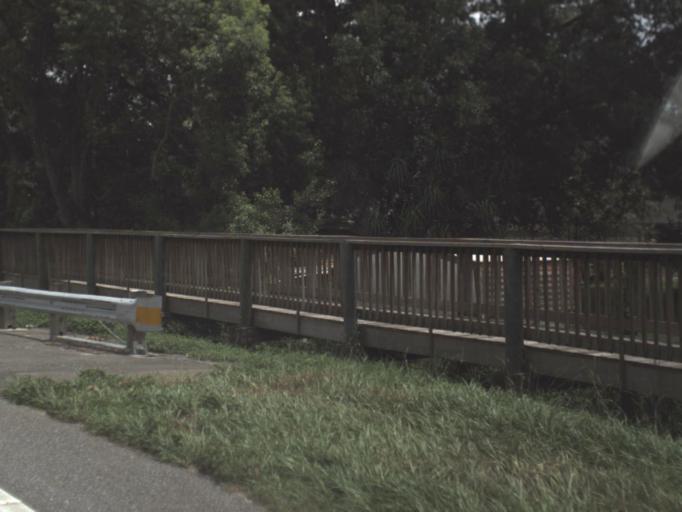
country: US
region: Florida
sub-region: Hillsborough County
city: Seffner
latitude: 28.0088
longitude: -82.2679
